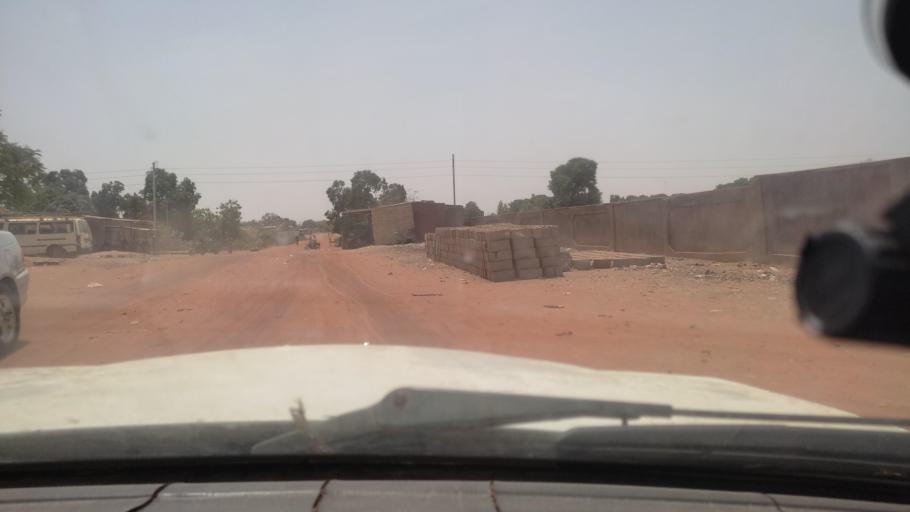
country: BF
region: Est
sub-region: Province du Gourma
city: Fada N'gourma
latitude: 12.0726
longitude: 0.3610
